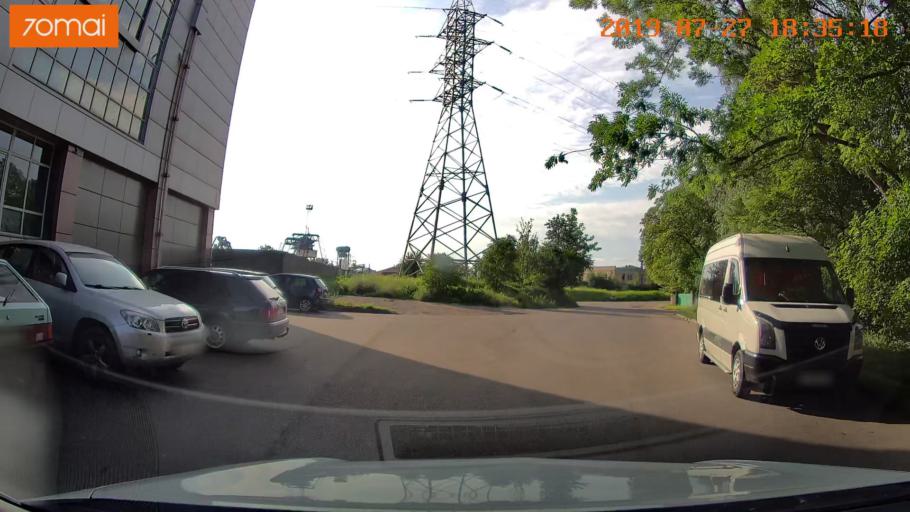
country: RU
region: Kaliningrad
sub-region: Gorod Kaliningrad
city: Kaliningrad
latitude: 54.7036
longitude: 20.4989
